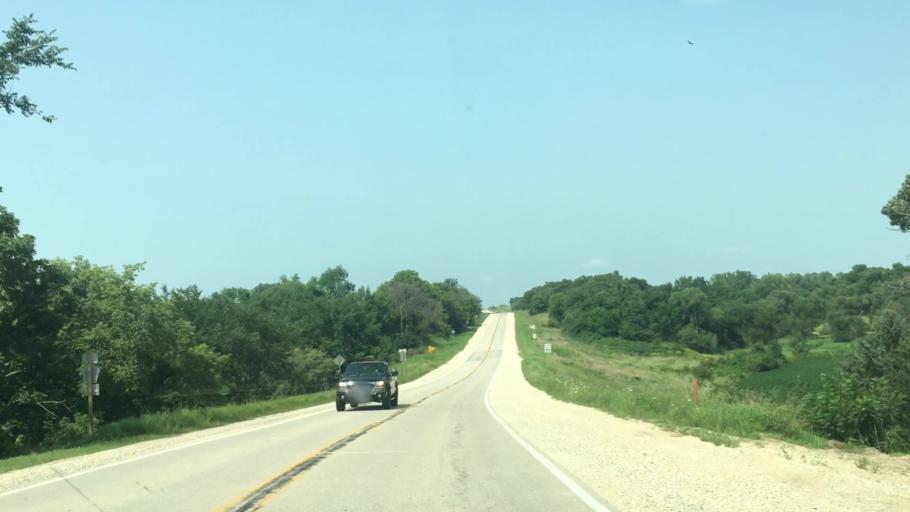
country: US
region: Iowa
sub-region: Fayette County
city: West Union
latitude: 43.1198
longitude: -91.8700
